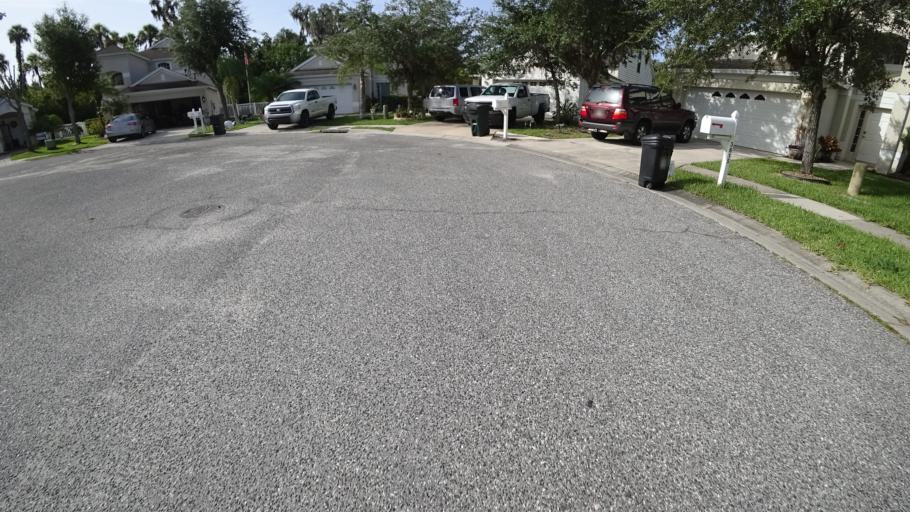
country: US
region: Florida
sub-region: Manatee County
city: Ellenton
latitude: 27.5477
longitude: -82.4970
